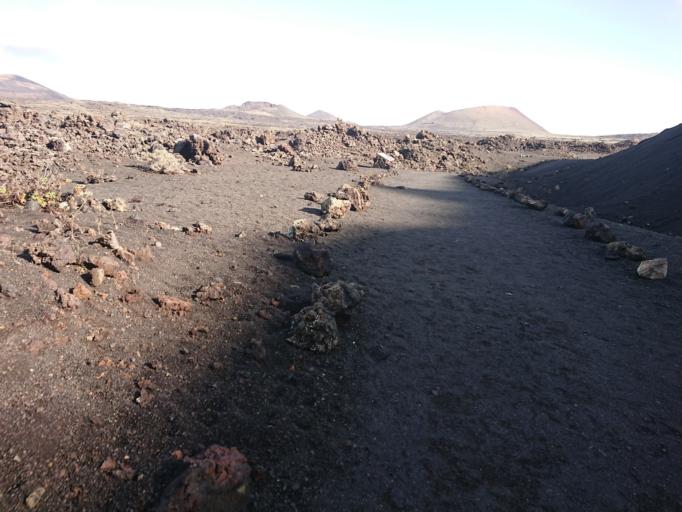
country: ES
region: Canary Islands
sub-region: Provincia de Las Palmas
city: Tias
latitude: 28.9925
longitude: -13.6950
